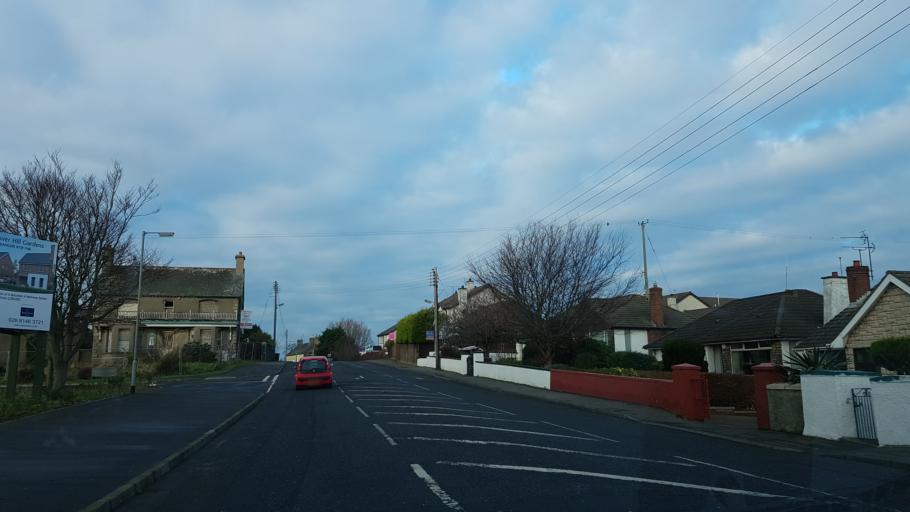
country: GB
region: Northern Ireland
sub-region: Down District
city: Donaghadee
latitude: 54.6387
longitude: -5.5333
